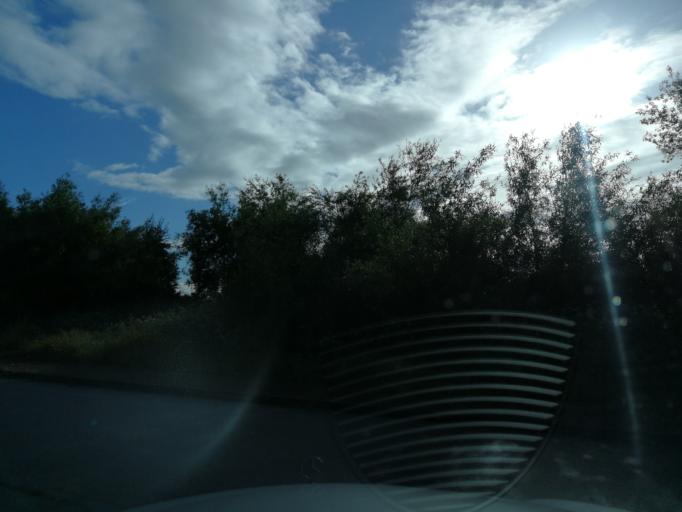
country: PT
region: Braga
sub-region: Braga
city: Braga
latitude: 41.5664
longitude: -8.4477
